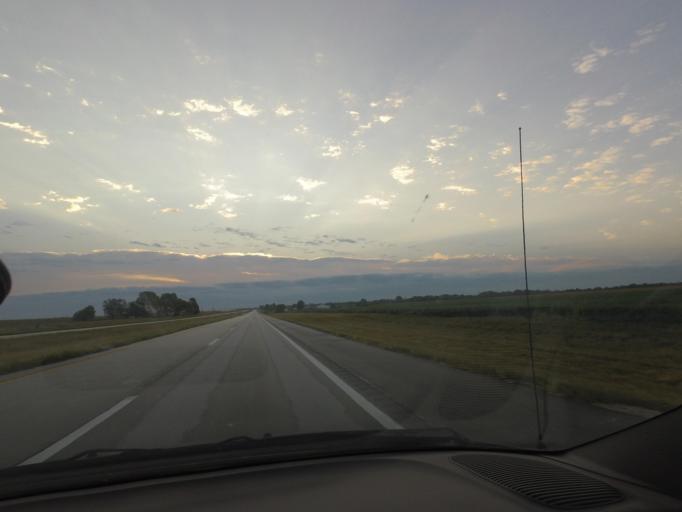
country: US
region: Missouri
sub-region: Macon County
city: Macon
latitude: 39.7505
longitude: -92.2898
